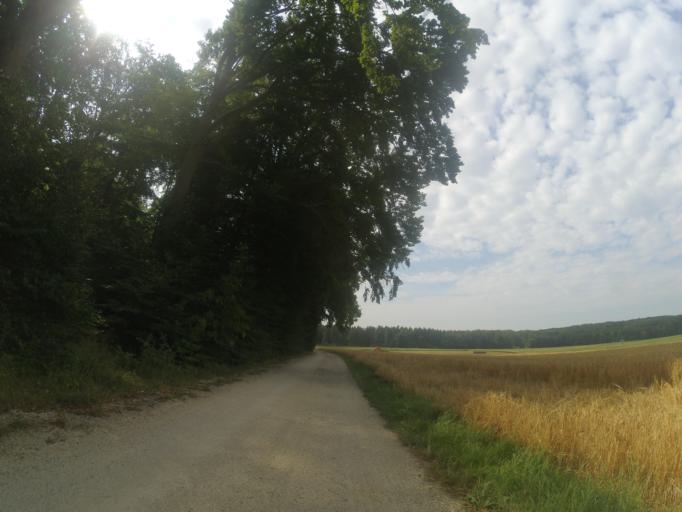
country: DE
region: Baden-Wuerttemberg
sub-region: Tuebingen Region
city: Lonsee
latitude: 48.5128
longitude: 9.8817
